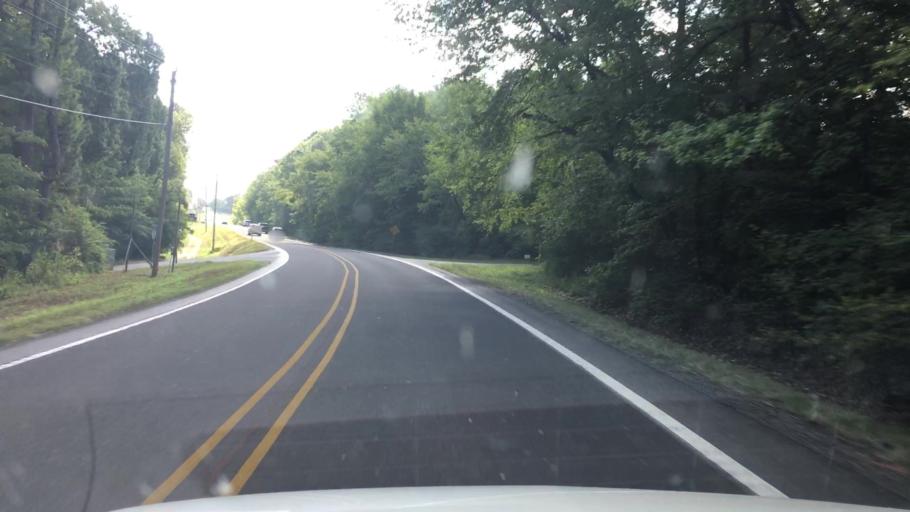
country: US
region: Arkansas
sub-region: Garland County
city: Piney
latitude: 34.5096
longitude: -93.1676
